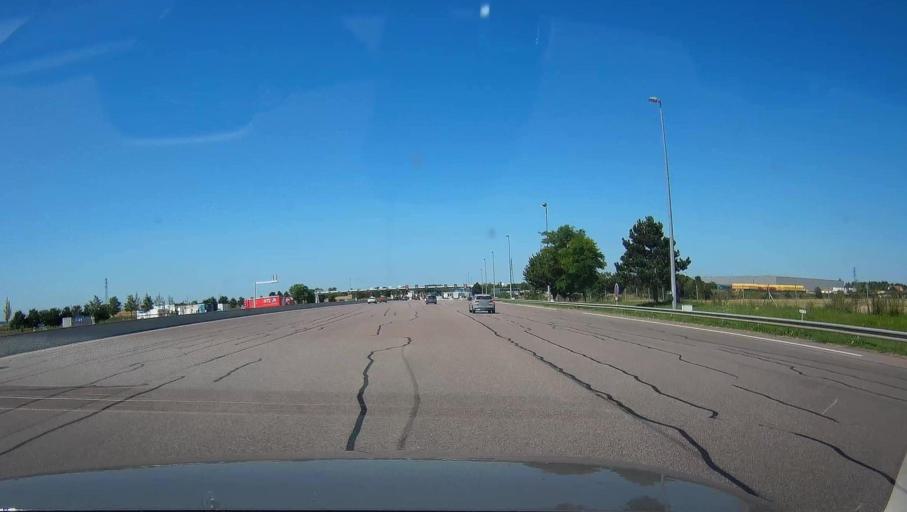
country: FR
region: Champagne-Ardenne
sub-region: Departement de la Marne
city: Taissy
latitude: 49.2094
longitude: 4.0816
